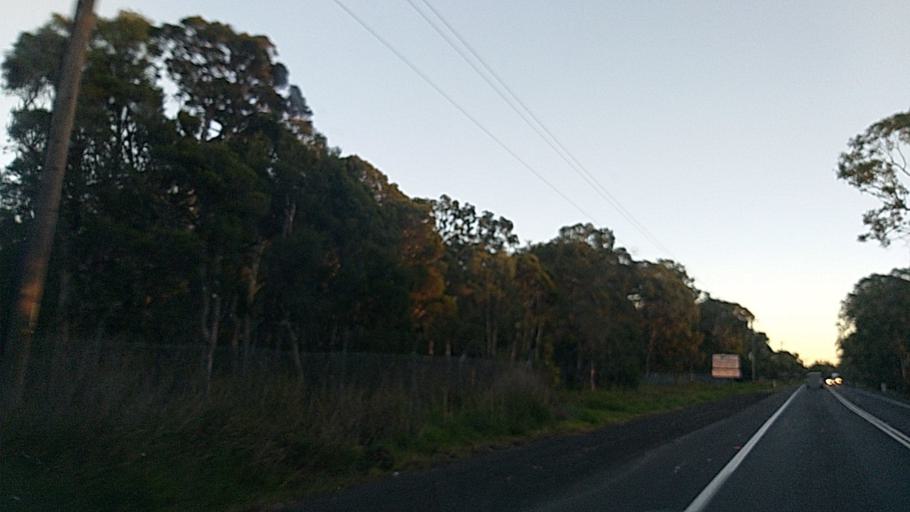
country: AU
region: New South Wales
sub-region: Hawkesbury
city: South Windsor
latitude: -33.6569
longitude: 150.7949
